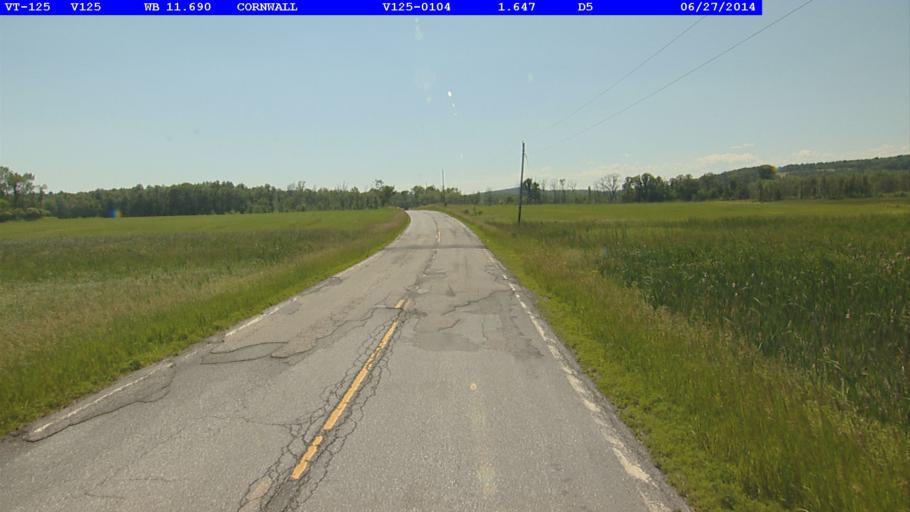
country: US
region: Vermont
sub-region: Addison County
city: Middlebury (village)
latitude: 43.9946
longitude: -73.2311
